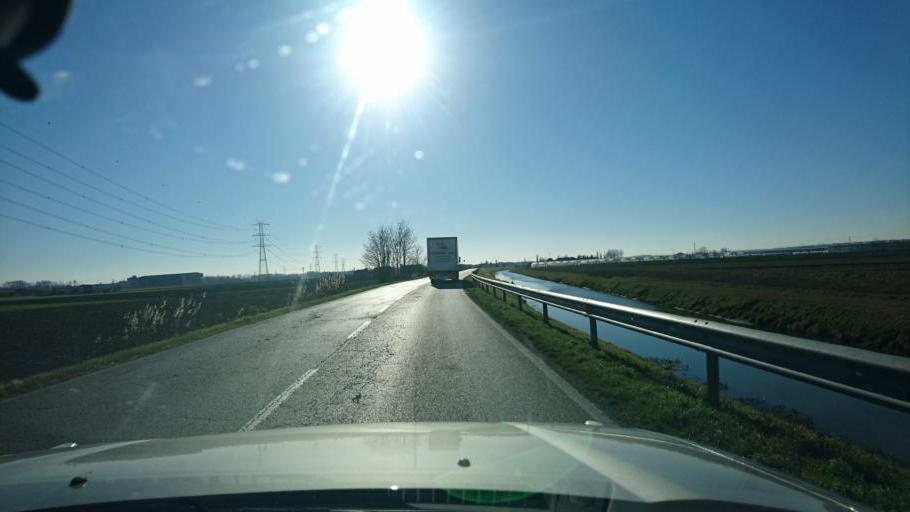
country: IT
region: Veneto
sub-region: Provincia di Rovigo
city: Taglio di Po
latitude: 44.9787
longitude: 12.2221
